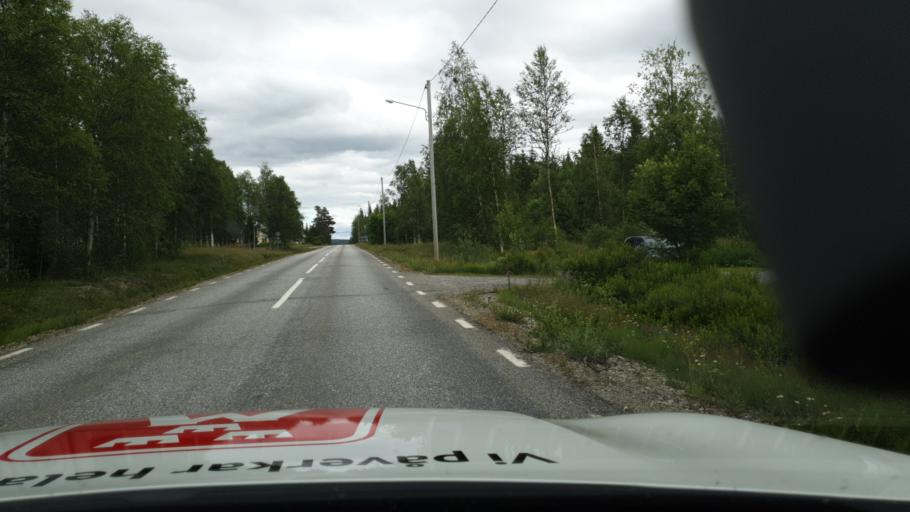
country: SE
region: Vaesterbotten
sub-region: Lycksele Kommun
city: Soderfors
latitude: 64.6420
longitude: 17.8712
